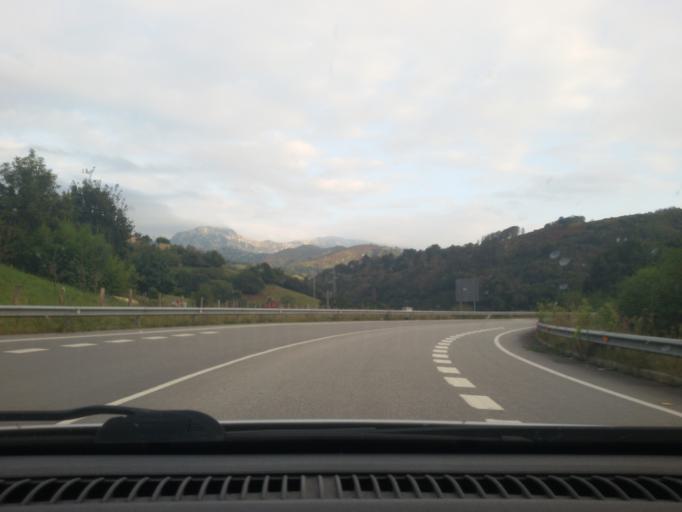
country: ES
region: Asturias
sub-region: Province of Asturias
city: Bimenes
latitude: 43.3421
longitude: -5.5801
